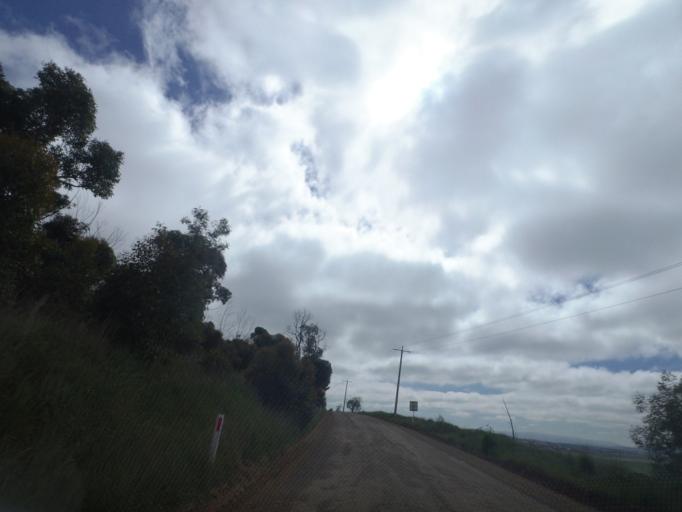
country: AU
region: Victoria
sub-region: Hume
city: Craigieburn
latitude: -37.4872
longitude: 144.9149
